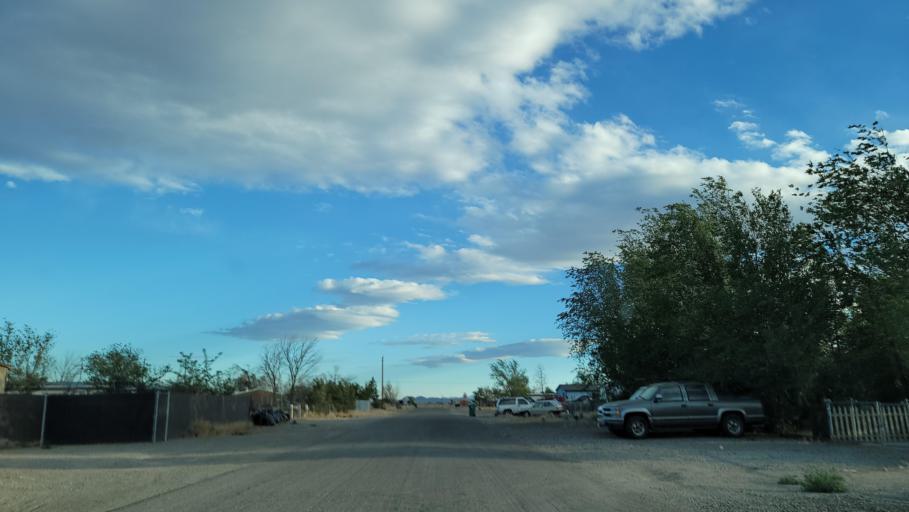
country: US
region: Nevada
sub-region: Lyon County
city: Silver Springs
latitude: 39.4067
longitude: -119.2225
